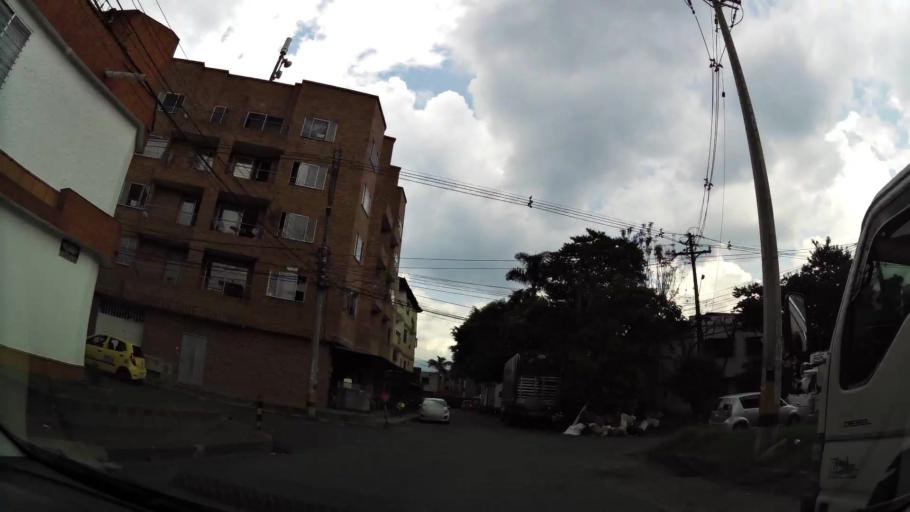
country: CO
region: Antioquia
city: Envigado
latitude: 6.1775
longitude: -75.5955
